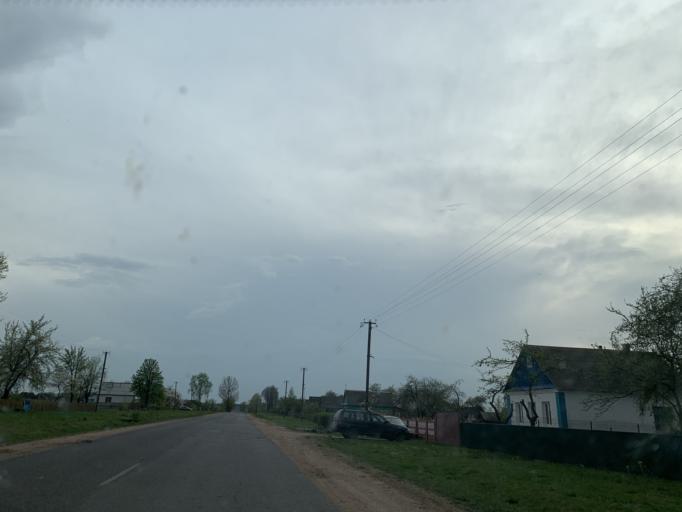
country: BY
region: Minsk
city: Kapyl'
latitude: 53.2740
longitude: 26.9673
